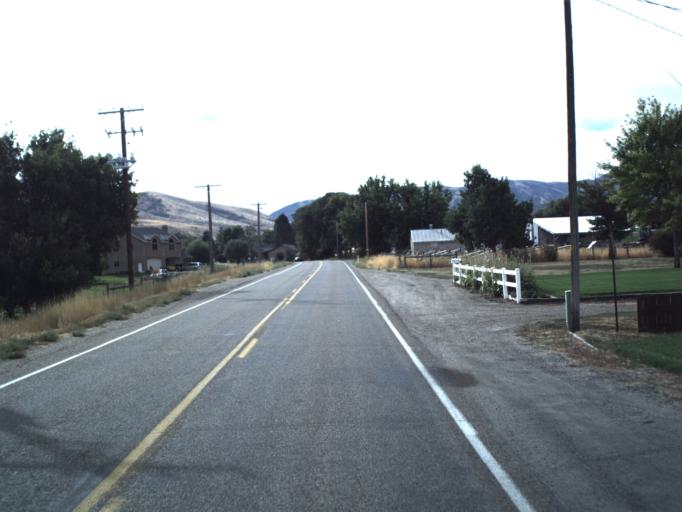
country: US
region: Utah
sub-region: Morgan County
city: Morgan
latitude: 40.9803
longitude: -111.6776
